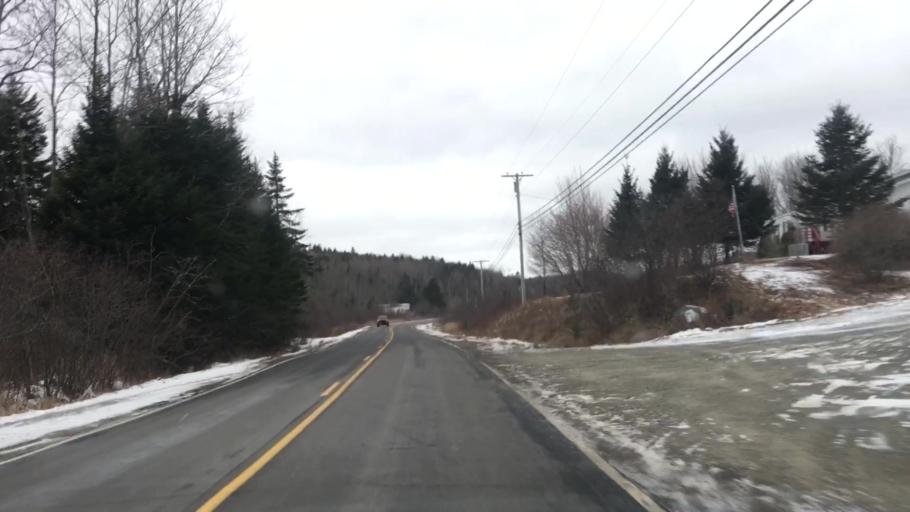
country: US
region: Maine
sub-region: Washington County
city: Machiasport
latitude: 44.7082
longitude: -67.3653
